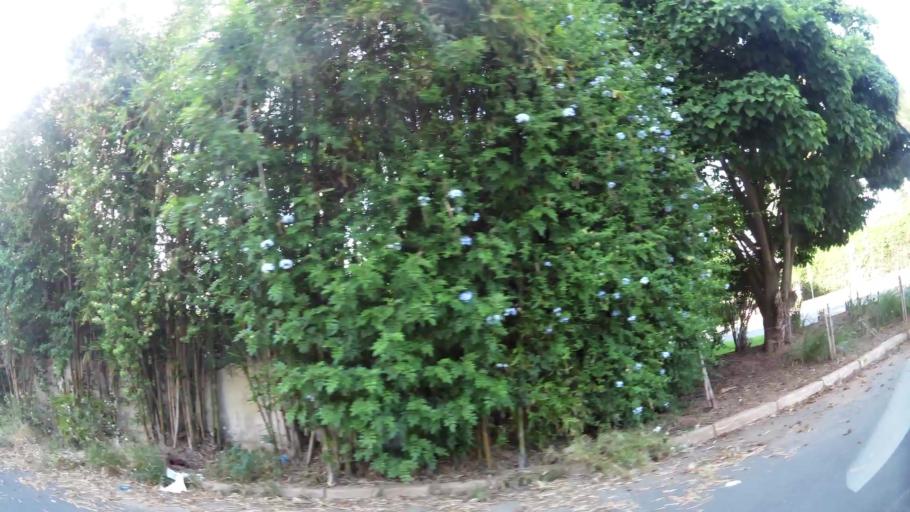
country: MA
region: Rabat-Sale-Zemmour-Zaer
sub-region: Rabat
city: Rabat
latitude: 33.9385
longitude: -6.8050
